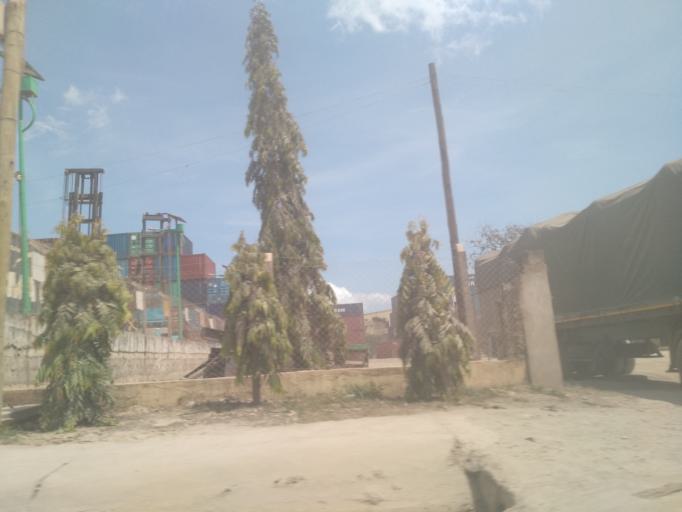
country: TZ
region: Dar es Salaam
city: Dar es Salaam
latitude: -6.8427
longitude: 39.2569
